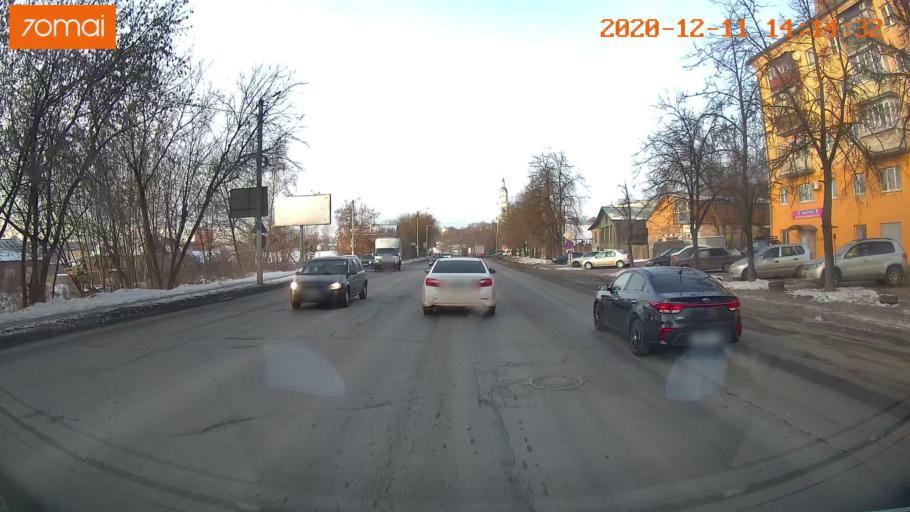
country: RU
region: Kostroma
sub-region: Kostromskoy Rayon
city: Kostroma
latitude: 57.7529
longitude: 40.9511
